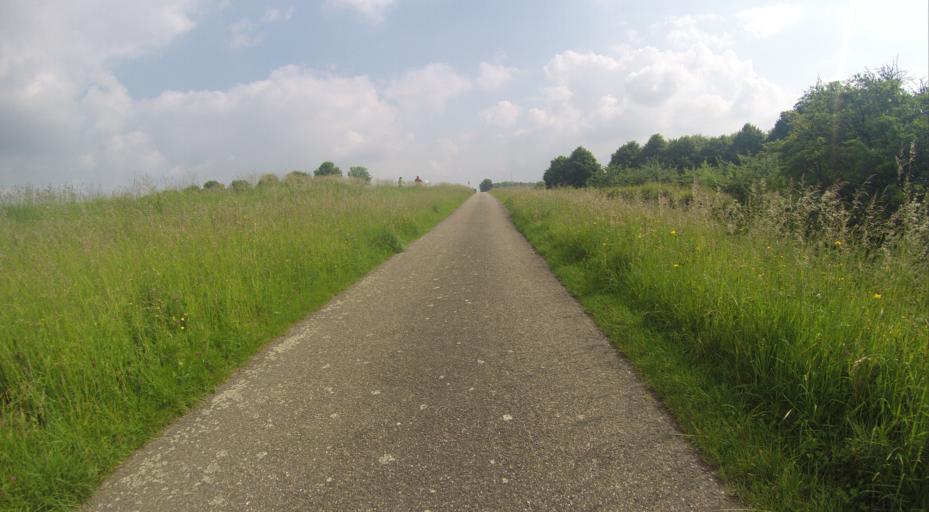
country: NL
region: Gelderland
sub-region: Gemeente Brummen
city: Brummen
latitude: 52.0763
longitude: 6.1761
